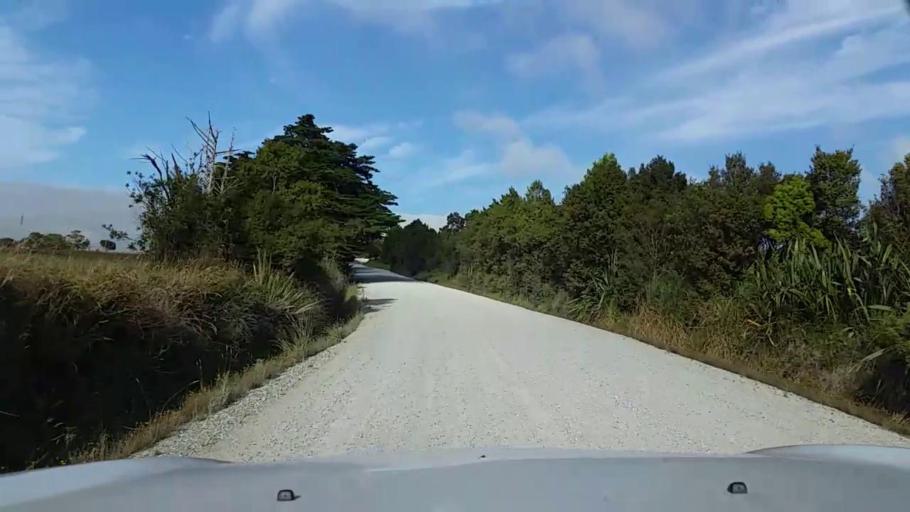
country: NZ
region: Northland
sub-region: Whangarei
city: Maungatapere
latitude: -35.6841
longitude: 174.1877
